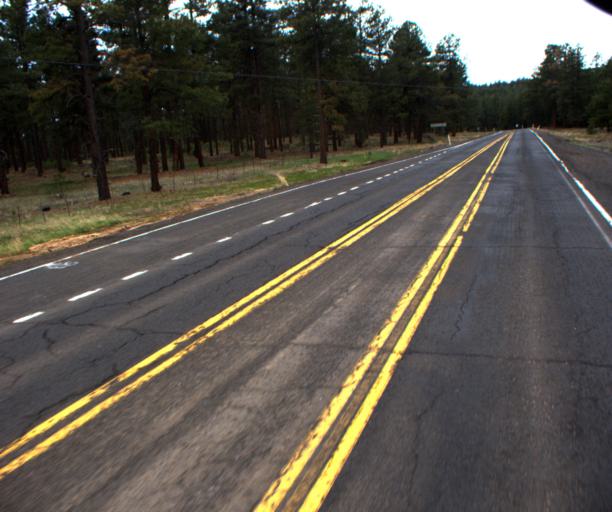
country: US
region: Arizona
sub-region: Coconino County
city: Kachina Village
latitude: 35.1216
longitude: -111.7036
